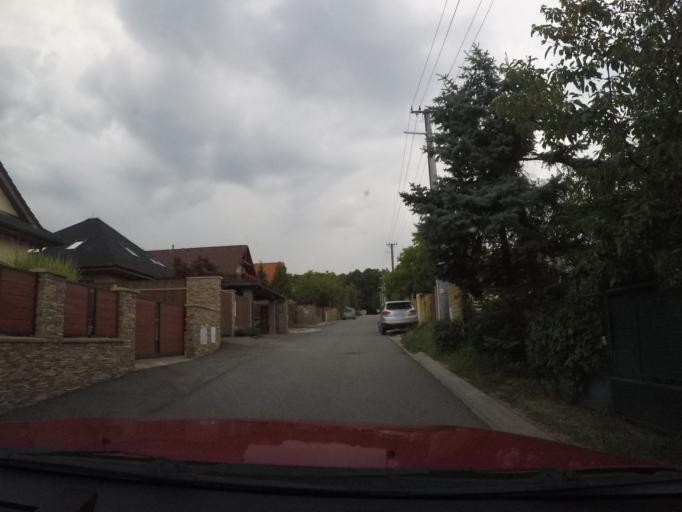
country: SK
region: Kosicky
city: Kosice
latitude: 48.6948
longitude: 21.2084
